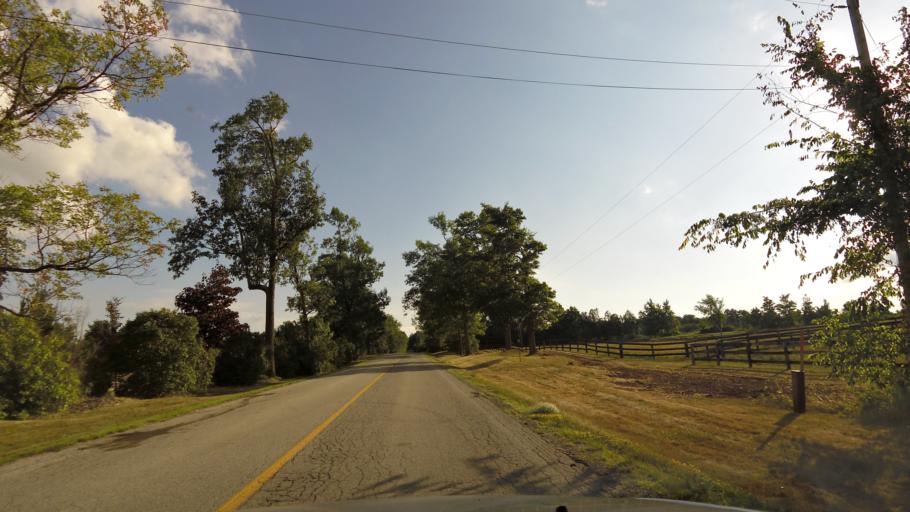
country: CA
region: Ontario
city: Brampton
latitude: 43.7554
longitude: -79.9465
